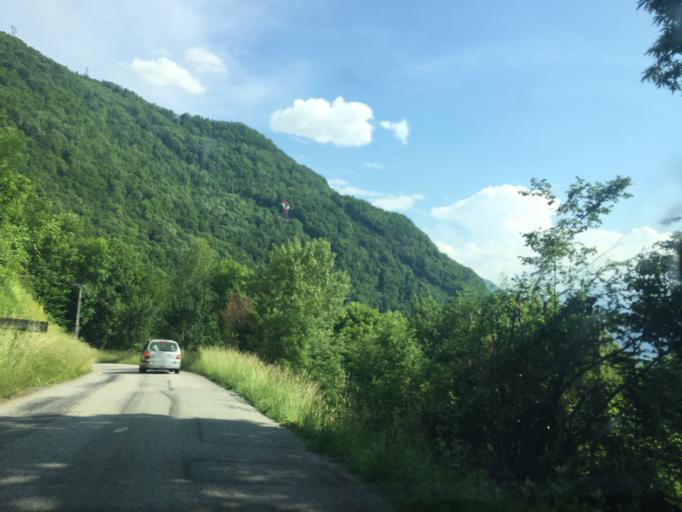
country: FR
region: Rhone-Alpes
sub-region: Departement de la Savoie
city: Aiton
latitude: 45.5340
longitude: 6.3231
